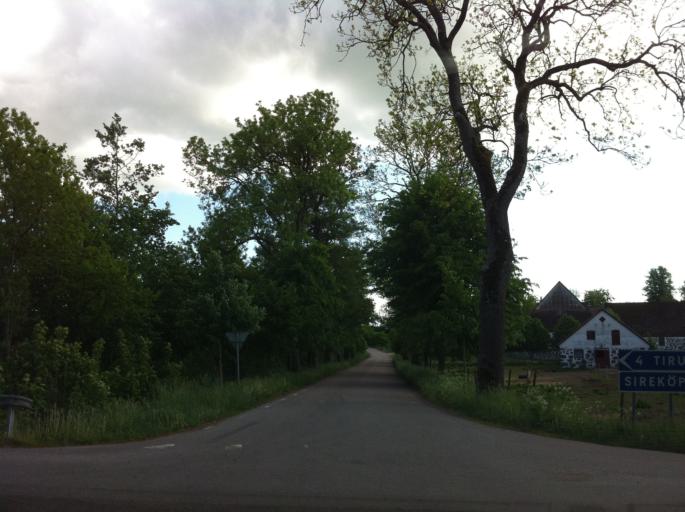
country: SE
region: Skane
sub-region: Svalovs Kommun
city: Kagerod
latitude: 56.0064
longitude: 13.0901
